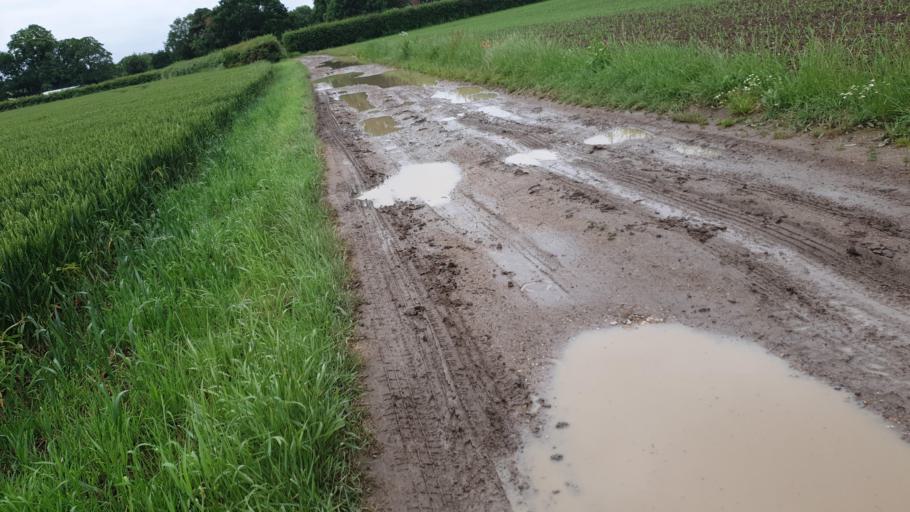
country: GB
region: England
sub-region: Essex
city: Great Bentley
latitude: 51.8811
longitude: 1.0595
